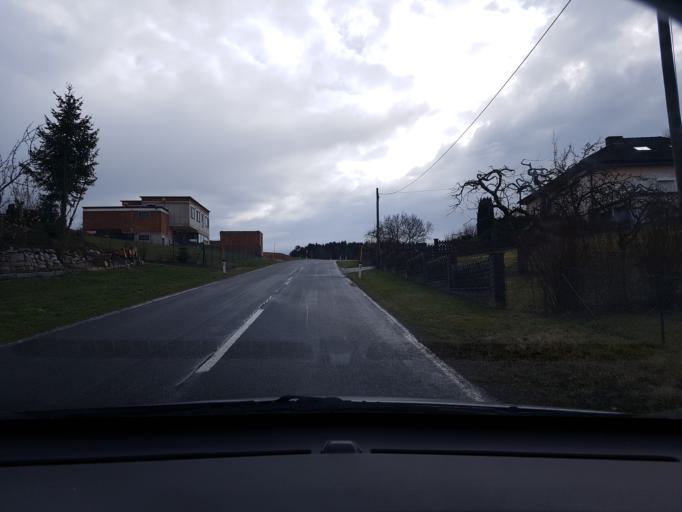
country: AT
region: Upper Austria
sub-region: Politischer Bezirk Linz-Land
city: Sankt Florian
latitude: 48.1530
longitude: 14.3587
